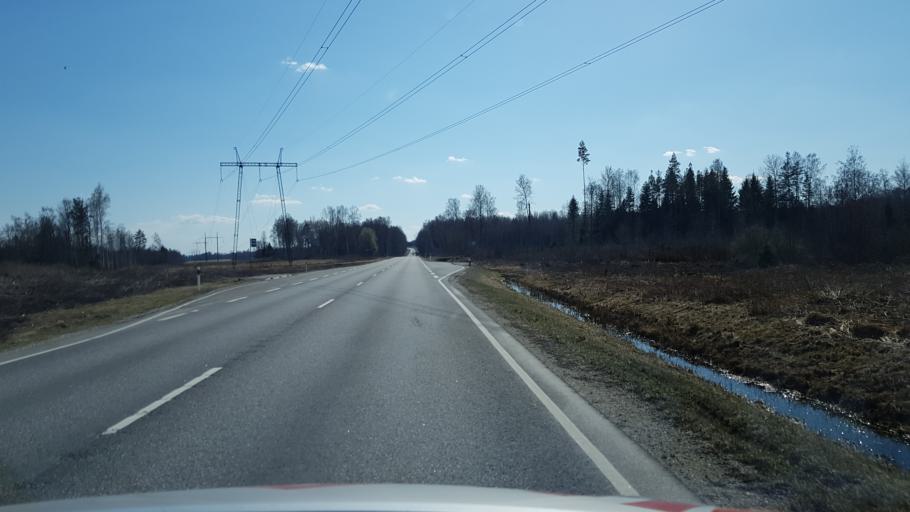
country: EE
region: Jogevamaa
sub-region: Mustvee linn
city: Mustvee
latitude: 58.6845
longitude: 26.8046
